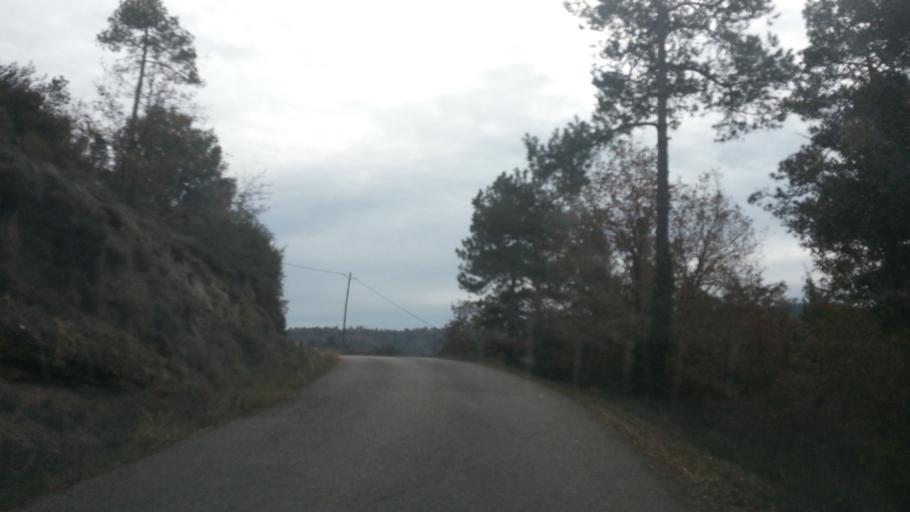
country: ES
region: Catalonia
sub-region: Provincia de Barcelona
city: Capolat
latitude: 41.9880
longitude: 1.7647
